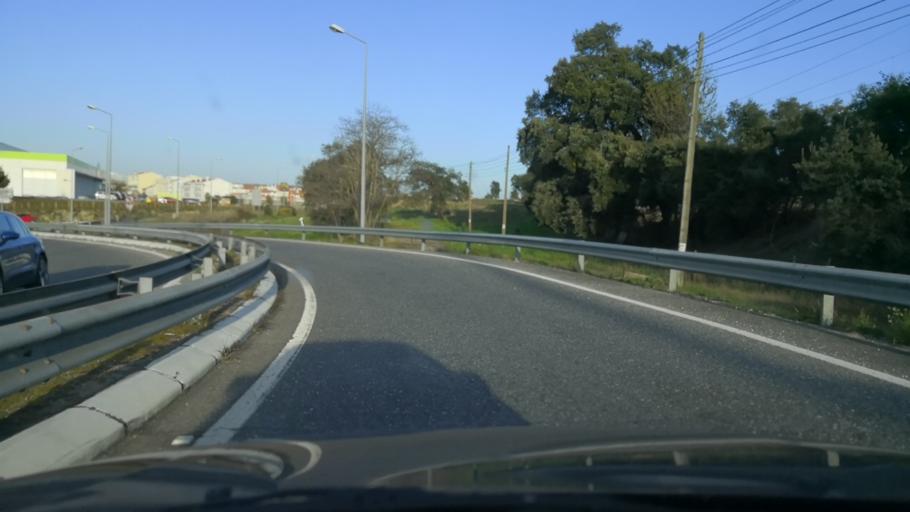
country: PT
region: Castelo Branco
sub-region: Castelo Branco
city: Castelo Branco
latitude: 39.8052
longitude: -7.5158
